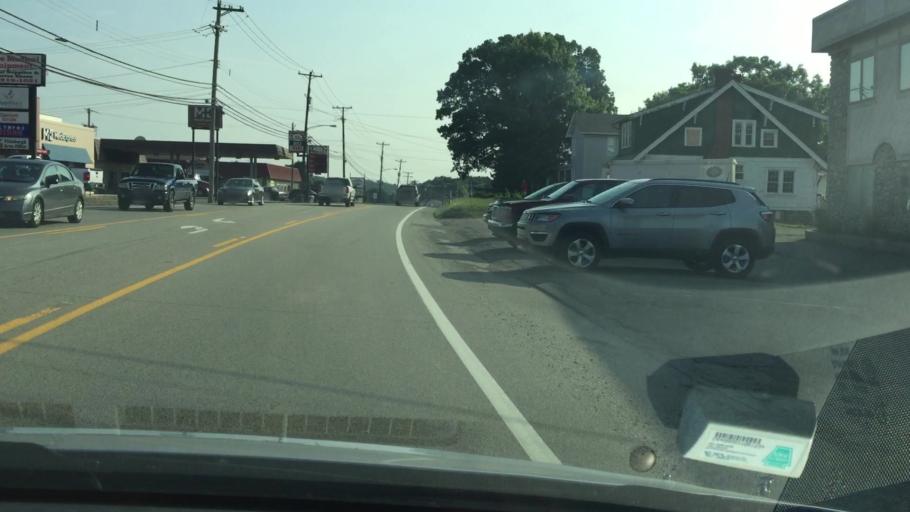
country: US
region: Pennsylvania
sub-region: Allegheny County
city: Rennerdale
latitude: 40.4476
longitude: -80.1430
